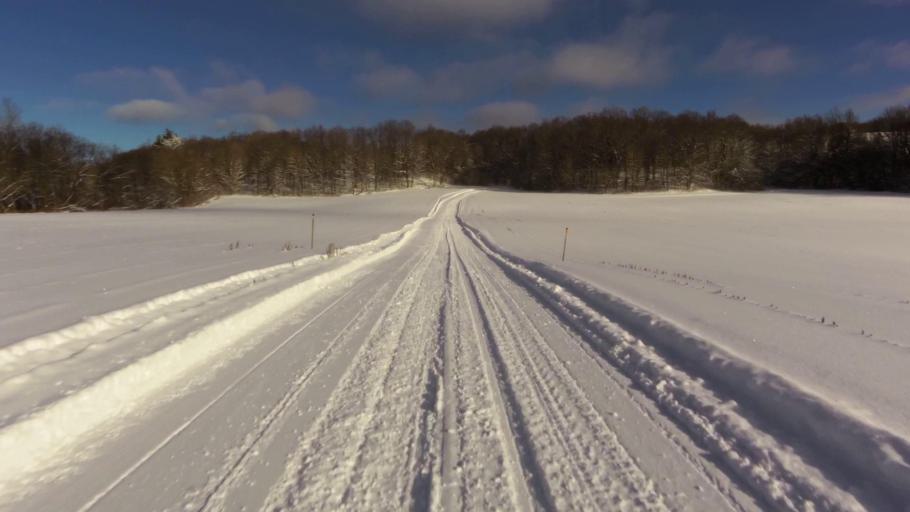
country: US
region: New York
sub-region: Chautauqua County
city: Falconer
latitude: 42.2518
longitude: -79.1439
